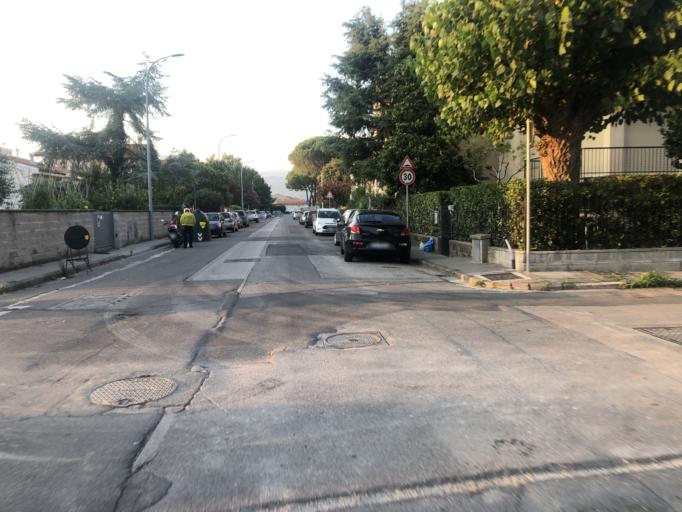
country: IT
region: Tuscany
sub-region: Province of Pisa
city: Pisa
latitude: 43.7257
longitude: 10.4091
